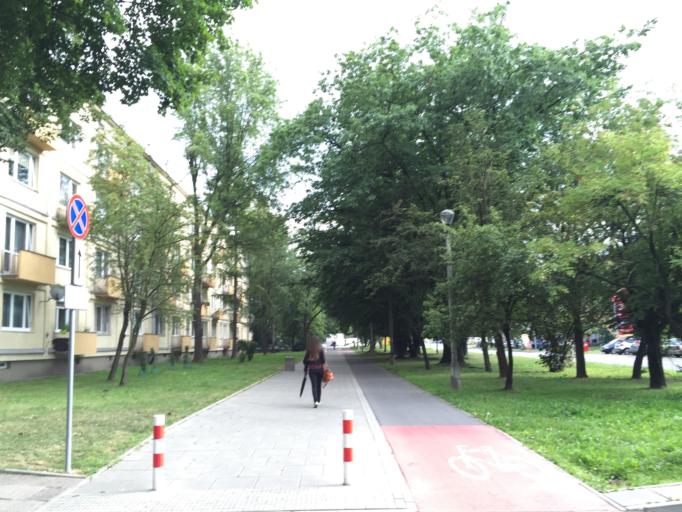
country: PL
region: Lesser Poland Voivodeship
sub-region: Powiat wielicki
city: Kokotow
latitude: 50.0737
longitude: 20.0298
